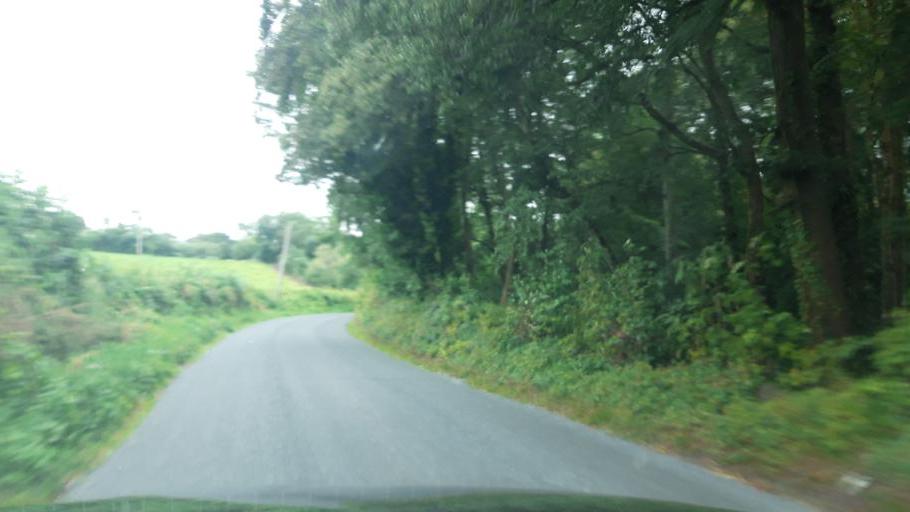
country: IE
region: Leinster
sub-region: Kilkenny
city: Ballyragget
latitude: 52.7241
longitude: -7.3999
